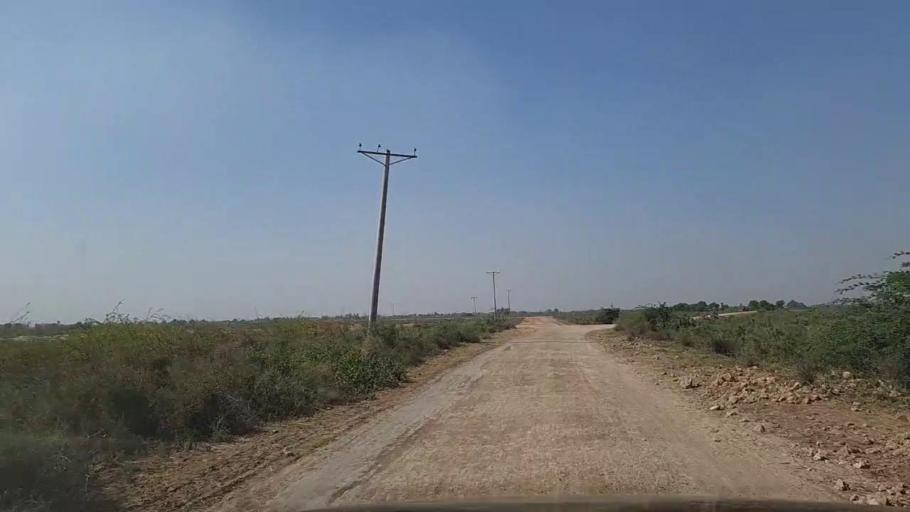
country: PK
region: Sindh
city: Daro Mehar
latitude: 24.8351
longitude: 68.1684
